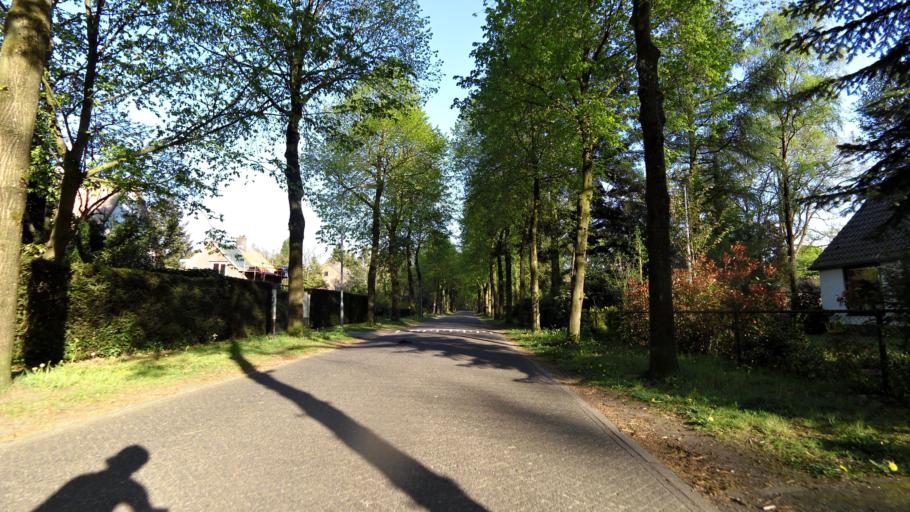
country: NL
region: Gelderland
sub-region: Gemeente Renkum
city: Wolfheze
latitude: 52.0079
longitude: 5.7908
